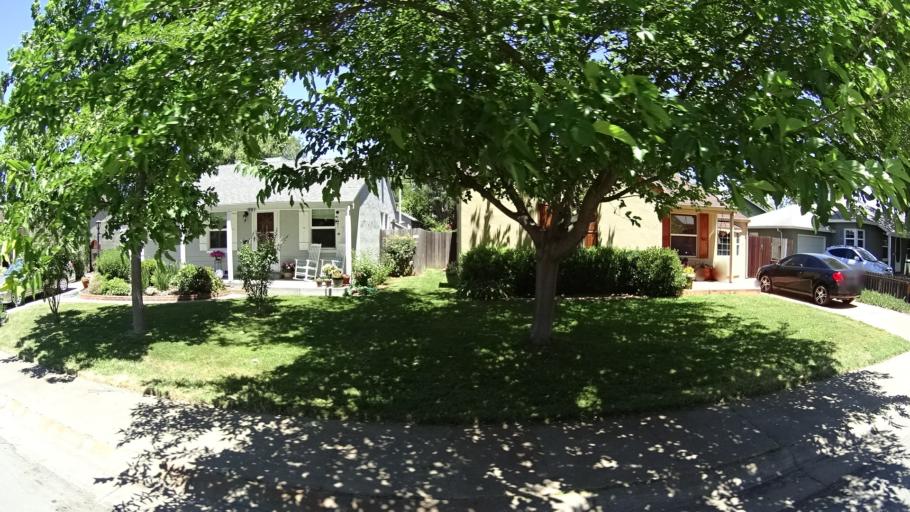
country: US
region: California
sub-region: Sacramento County
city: Sacramento
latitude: 38.5744
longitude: -121.4383
